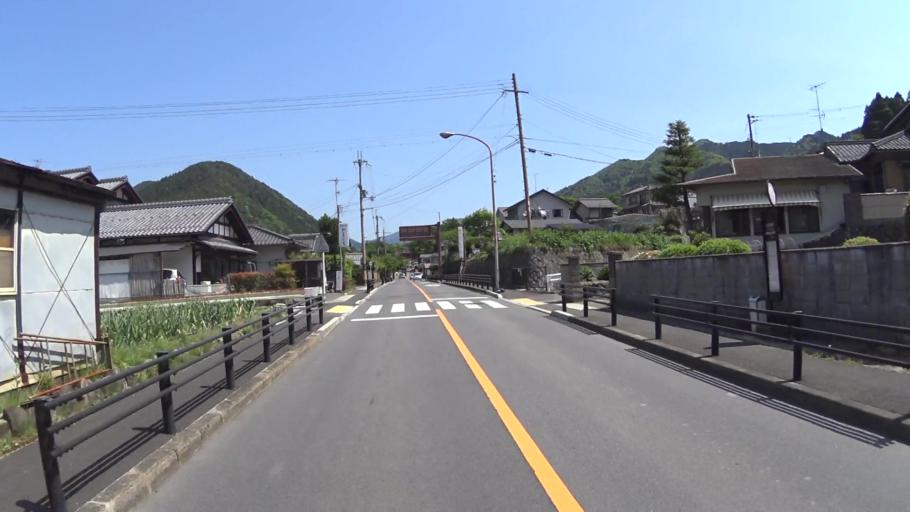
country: JP
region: Shiga Prefecture
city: Kitahama
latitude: 35.1145
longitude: 135.8266
